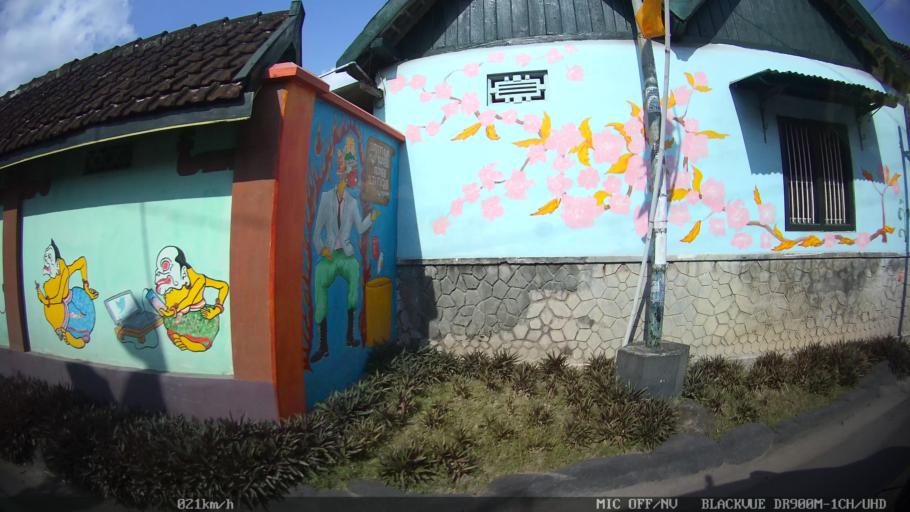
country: ID
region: Daerah Istimewa Yogyakarta
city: Yogyakarta
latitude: -7.8302
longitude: 110.3991
